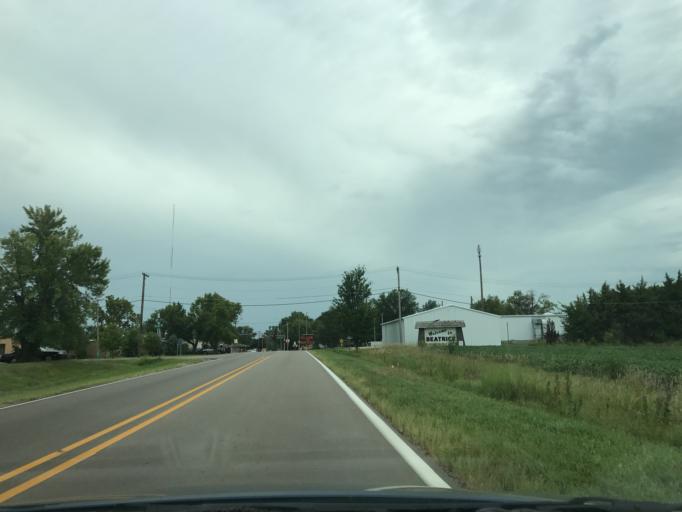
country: US
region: Nebraska
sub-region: Gage County
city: Beatrice
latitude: 40.2679
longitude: -96.7753
